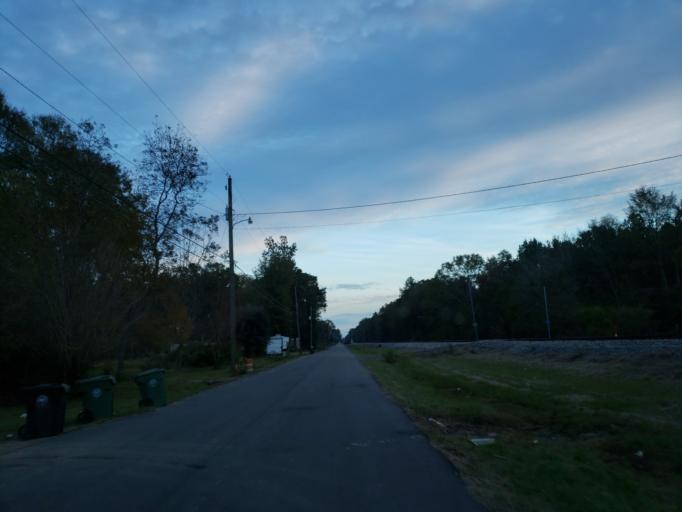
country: US
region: Mississippi
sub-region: Forrest County
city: Hattiesburg
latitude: 31.2785
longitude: -89.2555
